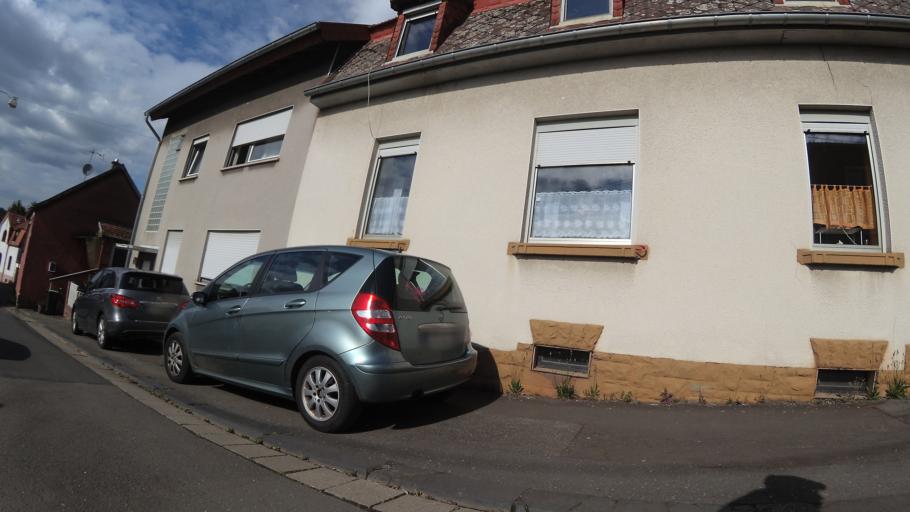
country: DE
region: Saarland
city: Hangard
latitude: 49.3666
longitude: 7.1931
